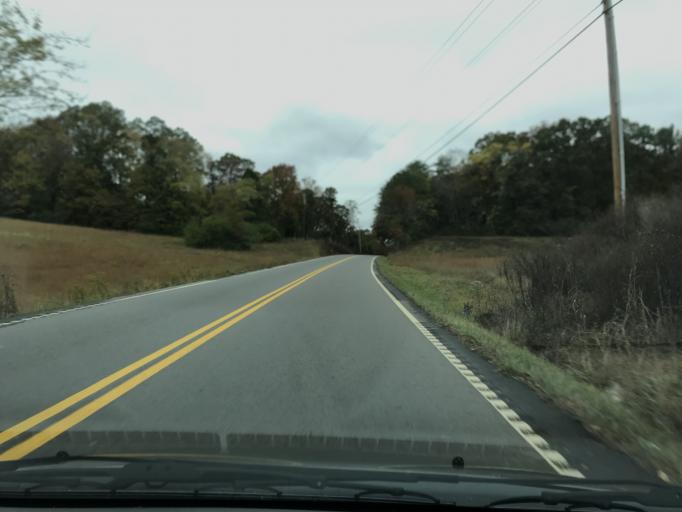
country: US
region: Tennessee
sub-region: Hamilton County
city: Sale Creek
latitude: 35.3499
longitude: -84.9862
